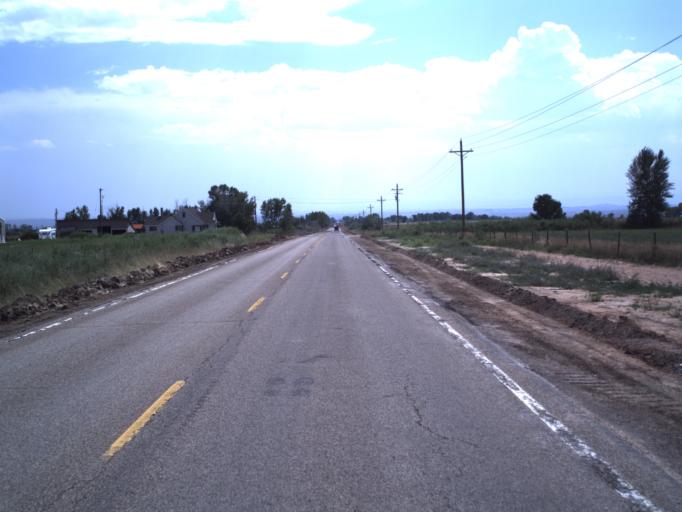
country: US
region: Utah
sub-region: Duchesne County
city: Roosevelt
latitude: 40.4197
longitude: -110.0300
